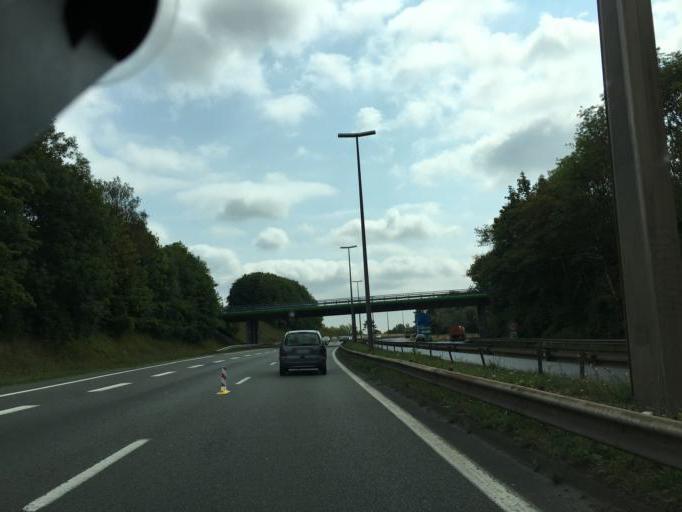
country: FR
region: Nord-Pas-de-Calais
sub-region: Departement du Pas-de-Calais
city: Loison-sous-Lens
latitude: 50.4442
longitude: 2.8430
